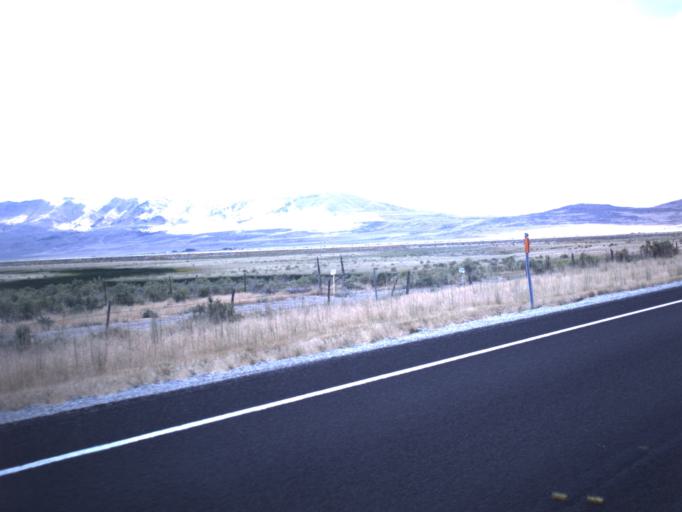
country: US
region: Utah
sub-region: Box Elder County
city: Tremonton
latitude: 41.6300
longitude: -112.4162
